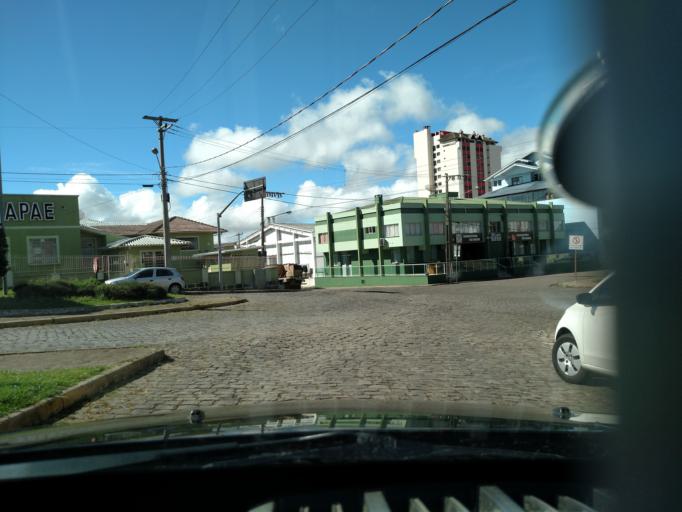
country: BR
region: Santa Catarina
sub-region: Sao Joaquim
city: Sao Joaquim
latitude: -28.2910
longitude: -49.9329
